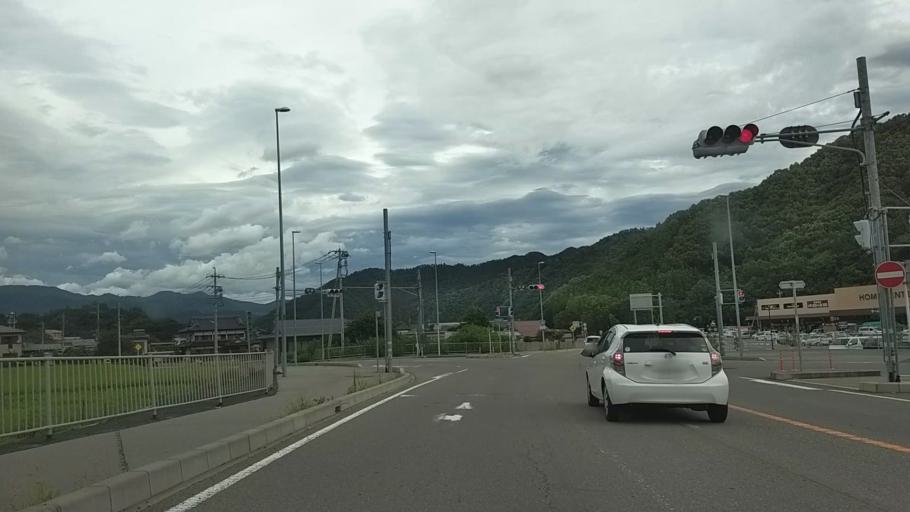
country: JP
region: Yamanashi
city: Otsuki
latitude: 35.5700
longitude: 138.9312
